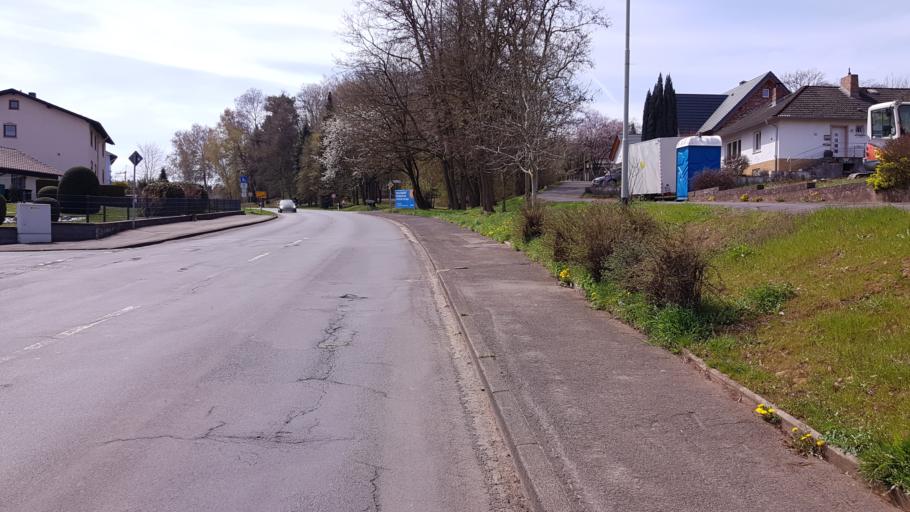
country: DE
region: Hesse
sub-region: Regierungsbezirk Giessen
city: Grunberg
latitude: 50.6433
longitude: 9.0303
